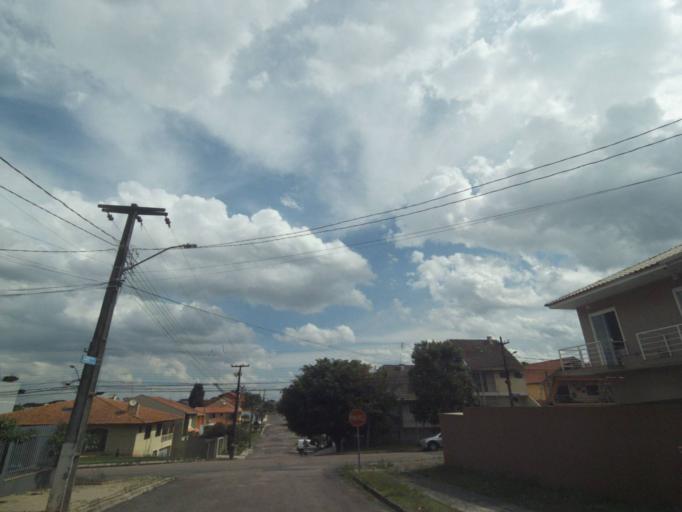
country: BR
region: Parana
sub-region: Curitiba
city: Curitiba
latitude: -25.4537
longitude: -49.3451
